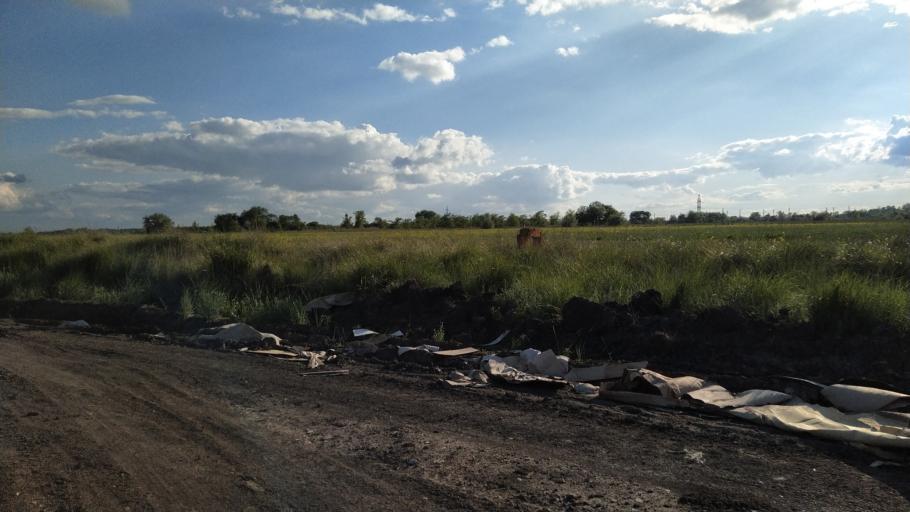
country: RU
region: Rostov
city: Bataysk
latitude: 47.1267
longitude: 39.7227
